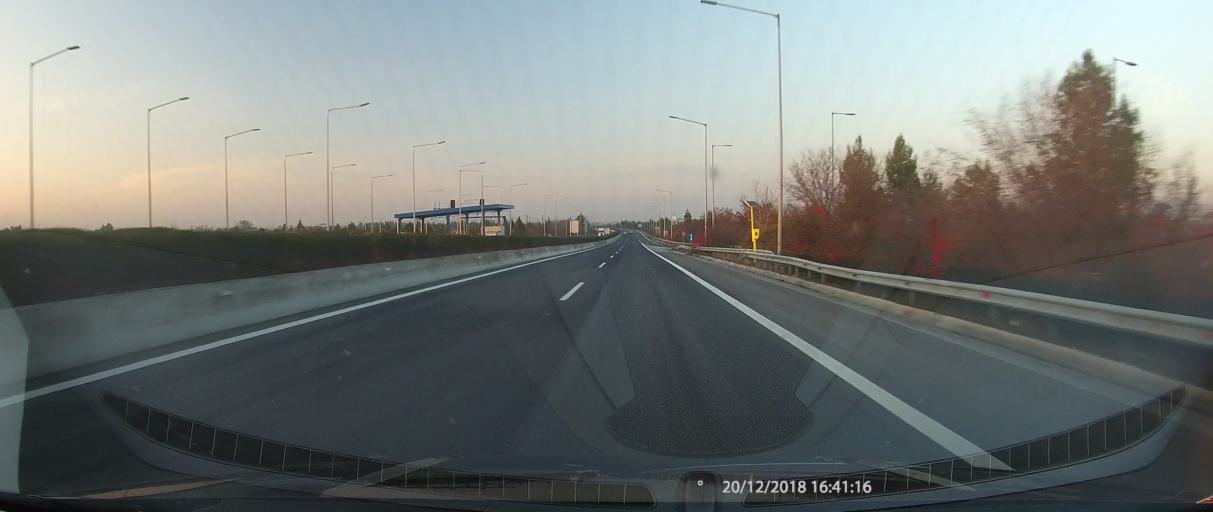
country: GR
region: Thessaly
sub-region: Nomos Magnisias
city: Velestino
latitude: 39.3895
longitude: 22.7657
